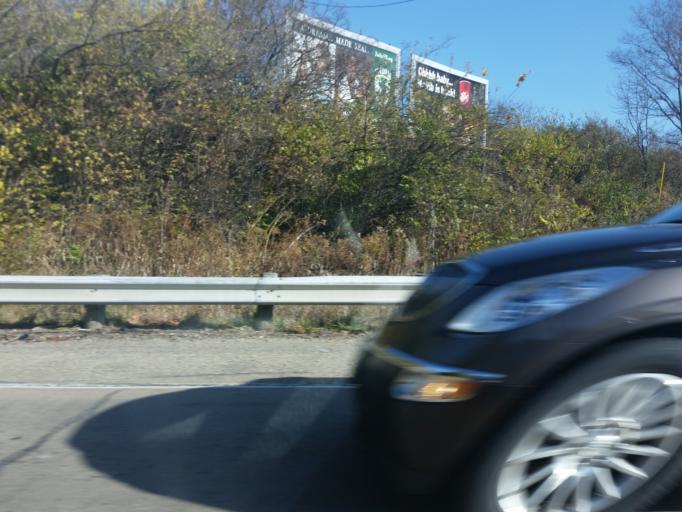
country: US
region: Ohio
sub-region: Butler County
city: Oxford
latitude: 39.4445
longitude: -84.6829
